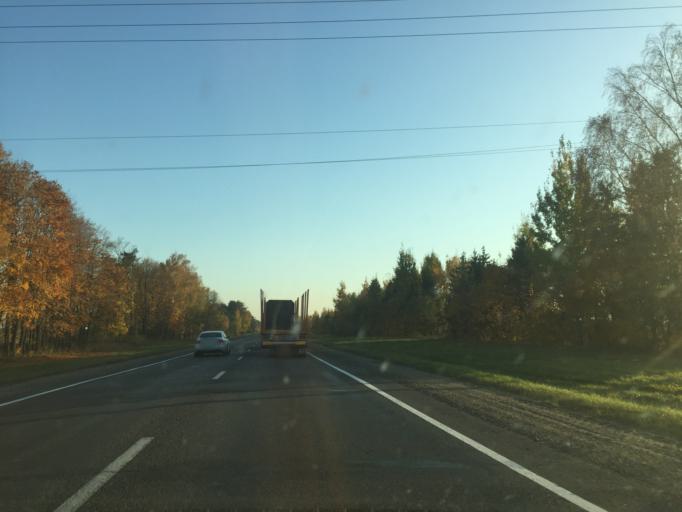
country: BY
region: Mogilev
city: Poselok Voskhod
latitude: 53.7487
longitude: 30.3656
